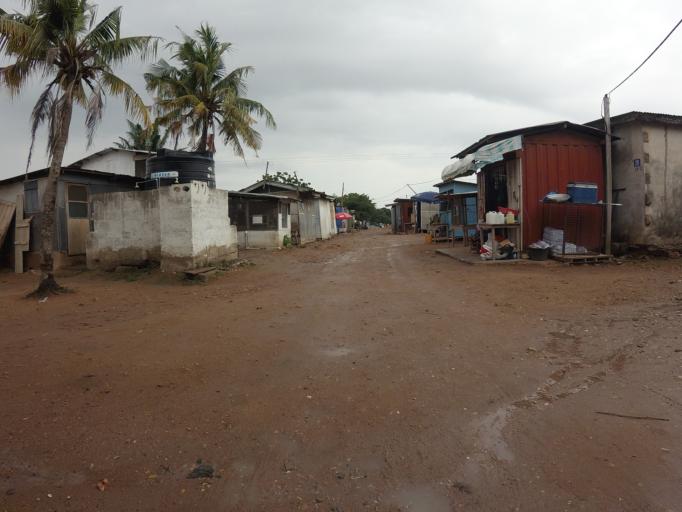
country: GH
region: Greater Accra
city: Dome
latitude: 5.6328
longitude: -0.2299
